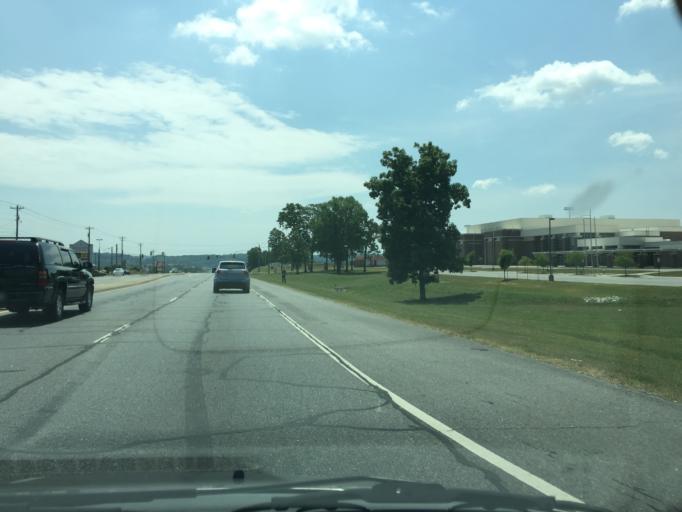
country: US
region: Georgia
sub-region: Catoosa County
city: Fort Oglethorpe
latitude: 34.9485
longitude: -85.2357
